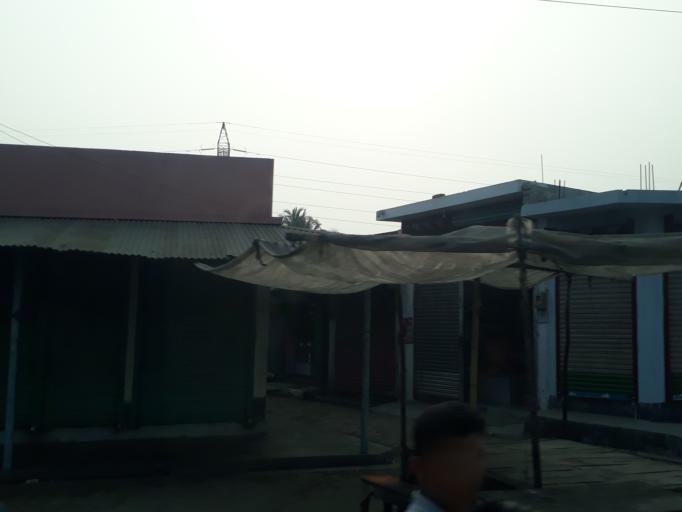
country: BD
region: Khulna
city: Bhatpara Abhaynagar
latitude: 22.9417
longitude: 89.4841
